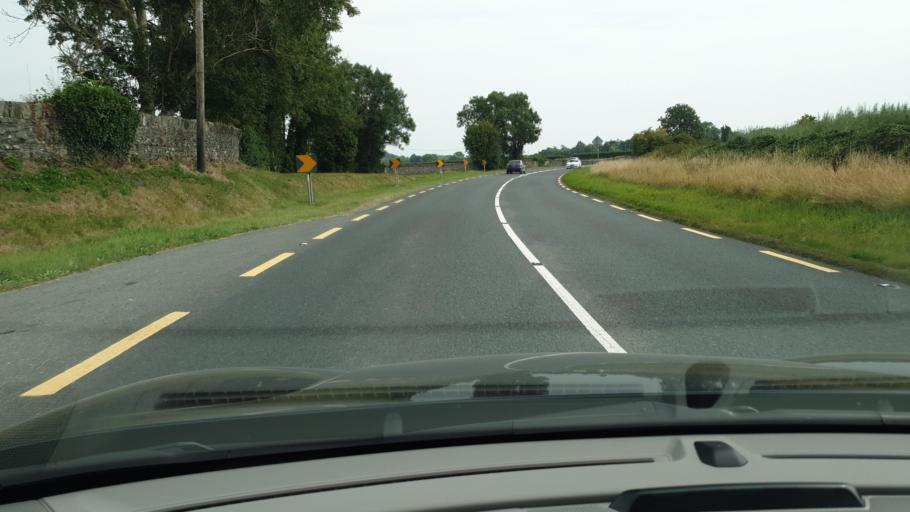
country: IE
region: Leinster
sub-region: An Mhi
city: Kells
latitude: 53.6994
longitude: -6.9406
